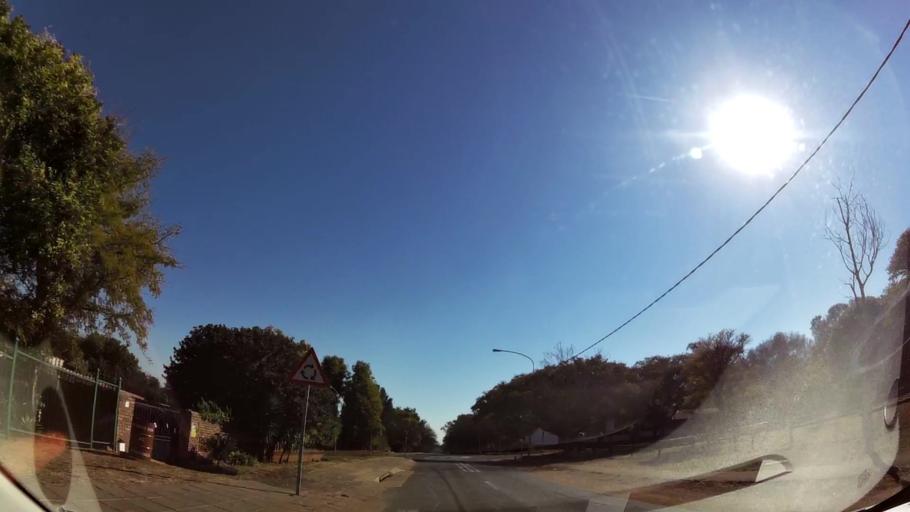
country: ZA
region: Gauteng
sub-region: City of Tshwane Metropolitan Municipality
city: Centurion
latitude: -25.8195
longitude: 28.2076
